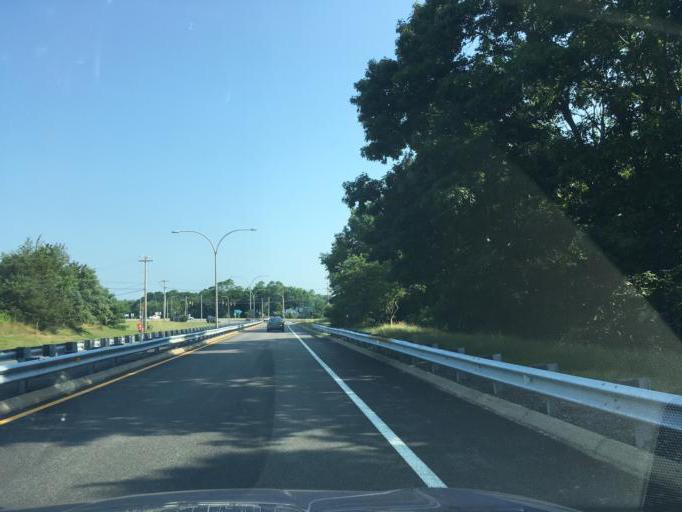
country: US
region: Rhode Island
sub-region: Washington County
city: Exeter
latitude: 41.5809
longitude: -71.4992
